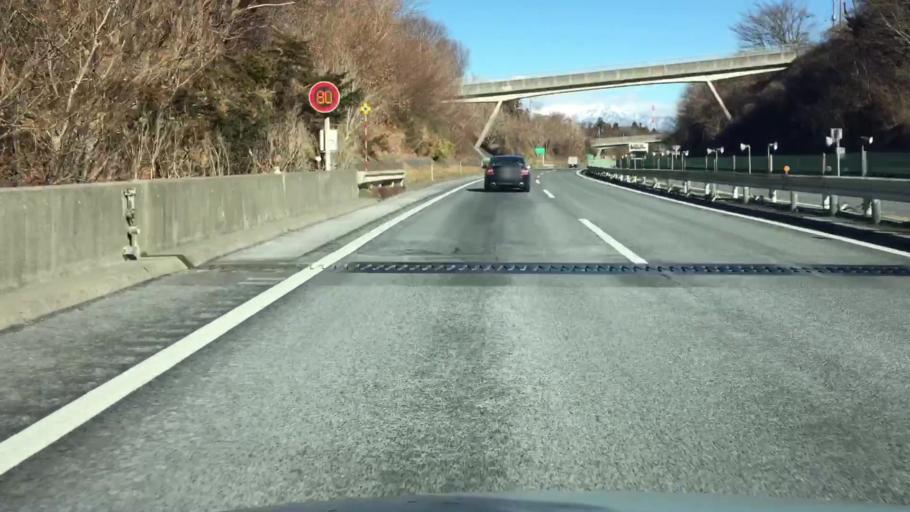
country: JP
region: Gunma
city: Numata
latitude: 36.5500
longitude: 139.0535
